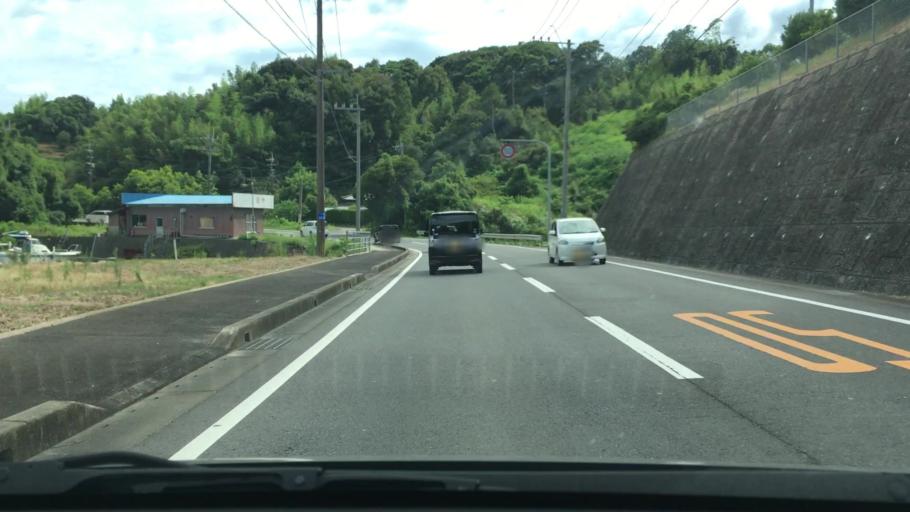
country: JP
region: Nagasaki
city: Togitsu
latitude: 32.9189
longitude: 129.7852
